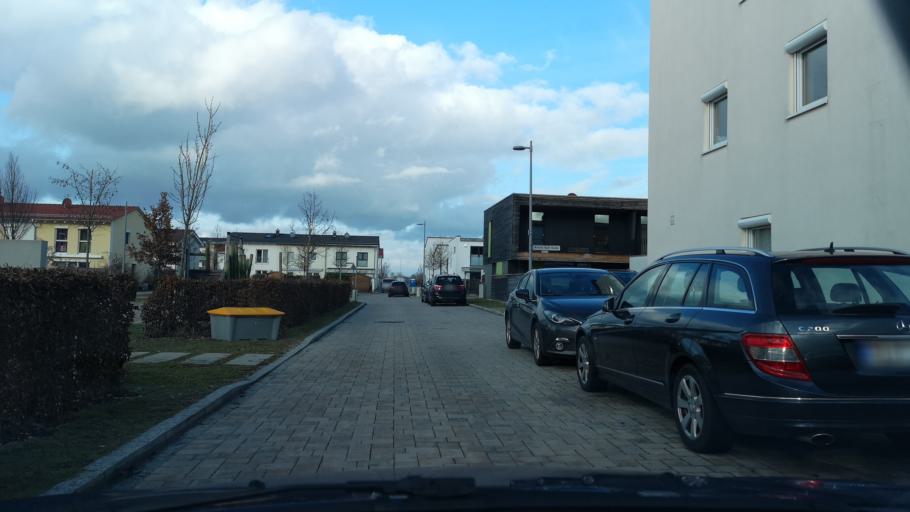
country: DE
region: Bavaria
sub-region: Upper Bavaria
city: Pliening
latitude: 48.1793
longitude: 11.8023
